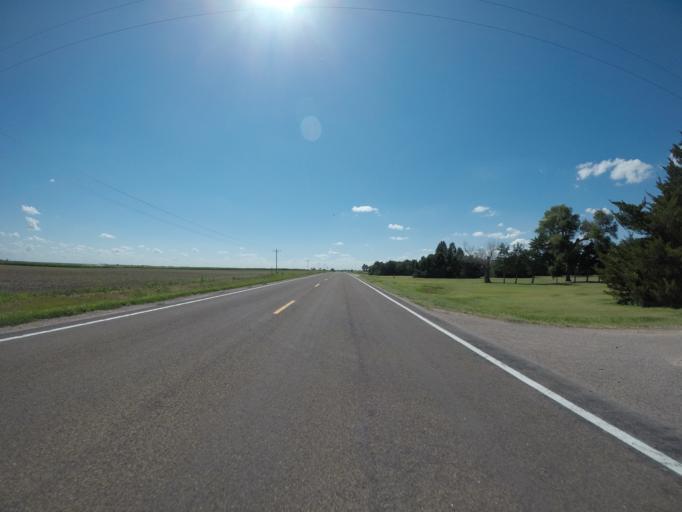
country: US
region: Nebraska
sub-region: Chase County
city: Imperial
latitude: 40.5376
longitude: -101.8075
